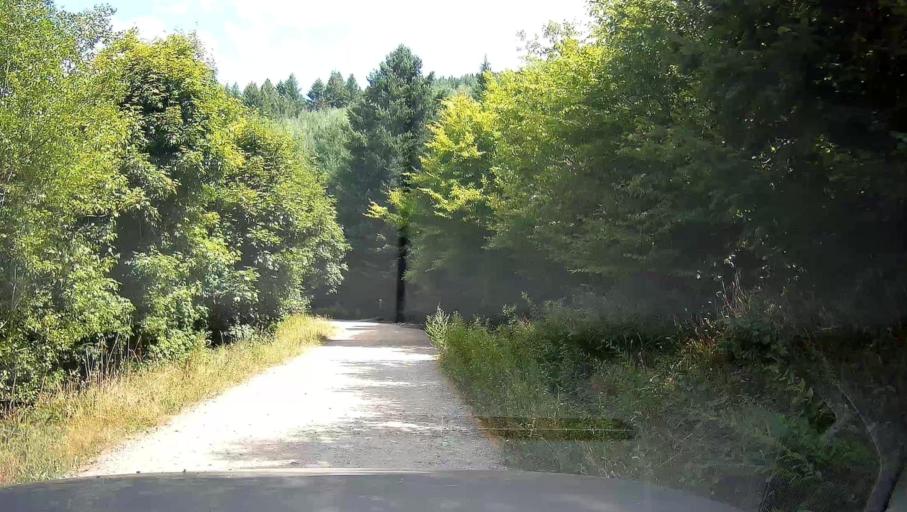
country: FR
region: Rhone-Alpes
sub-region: Departement du Rhone
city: Grandris
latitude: 46.0164
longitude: 4.5448
